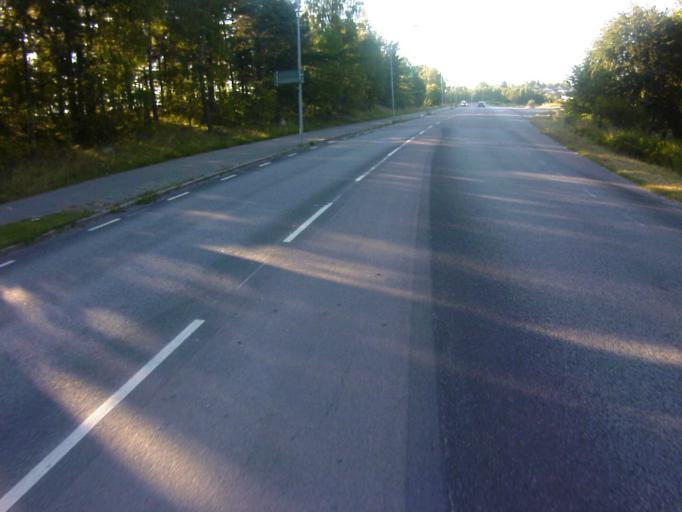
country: SE
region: Soedermanland
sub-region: Eskilstuna Kommun
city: Hallbybrunn
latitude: 59.3769
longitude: 16.4388
